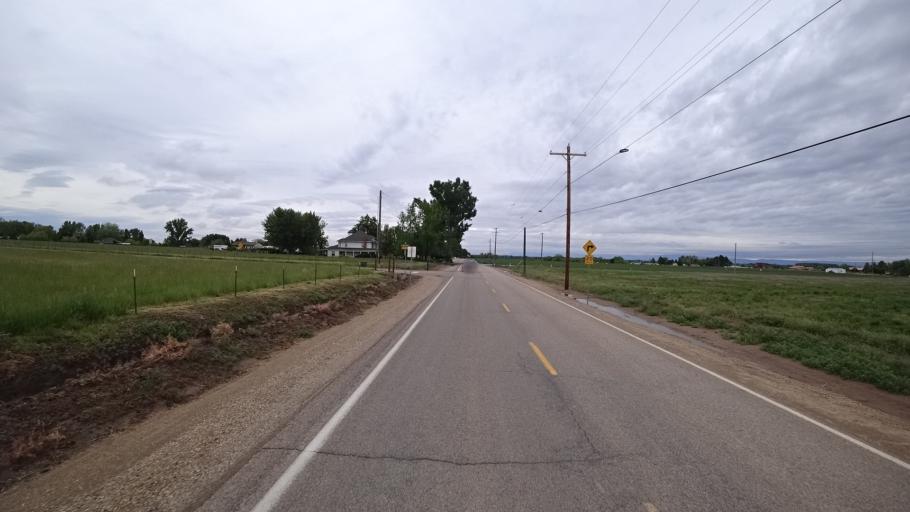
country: US
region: Idaho
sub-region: Ada County
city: Star
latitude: 43.7187
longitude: -116.4830
